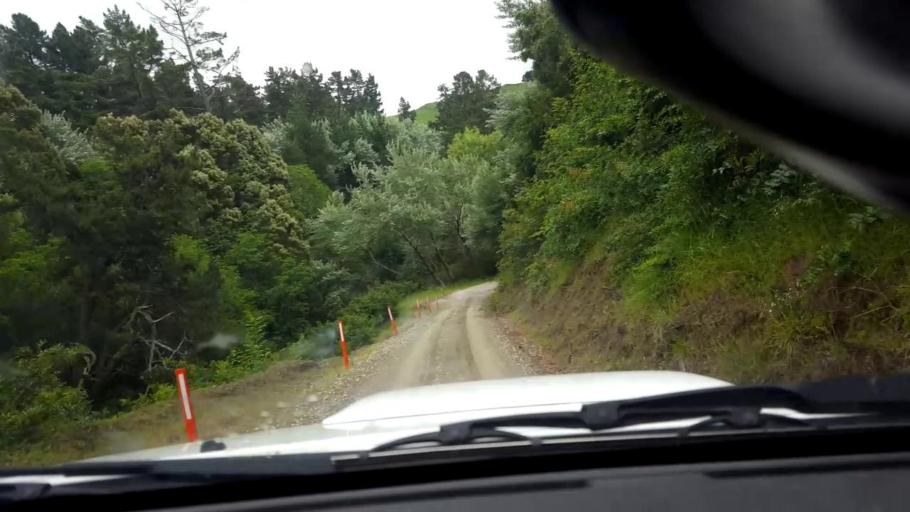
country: NZ
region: Gisborne
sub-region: Gisborne District
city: Gisborne
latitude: -38.3827
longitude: 177.6285
